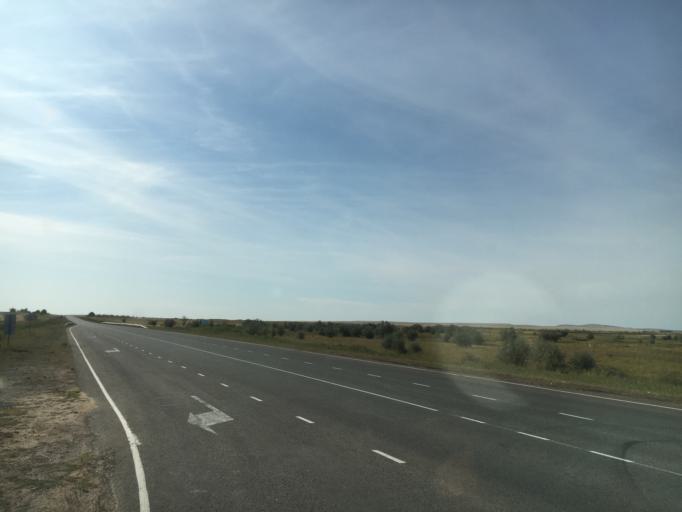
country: KZ
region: Batys Qazaqstan
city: Kamenka
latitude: 51.1071
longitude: 50.4120
